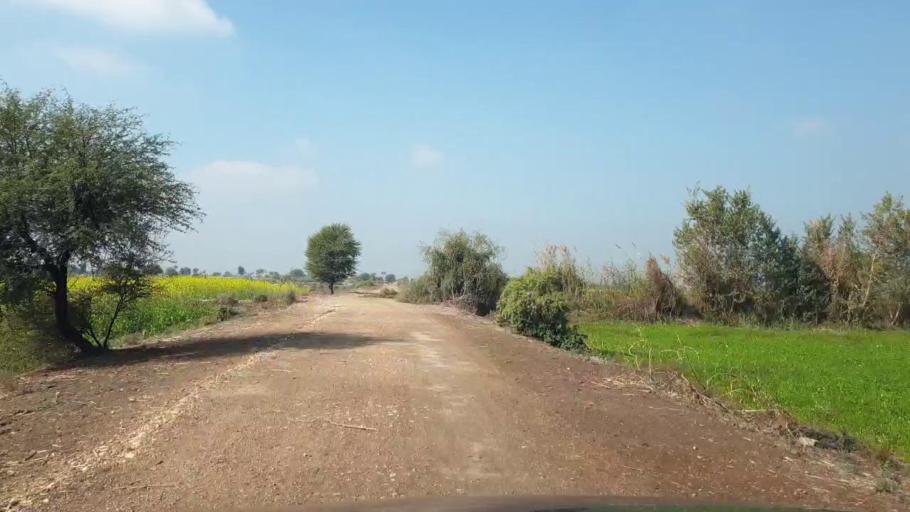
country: PK
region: Sindh
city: Sinjhoro
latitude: 26.0539
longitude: 68.7811
